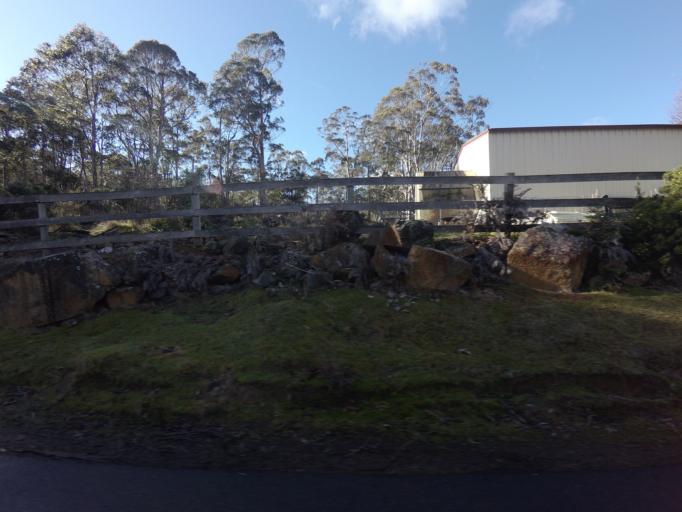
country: AU
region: Tasmania
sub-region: Glenorchy
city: Berriedale
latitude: -42.8436
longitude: 147.1662
